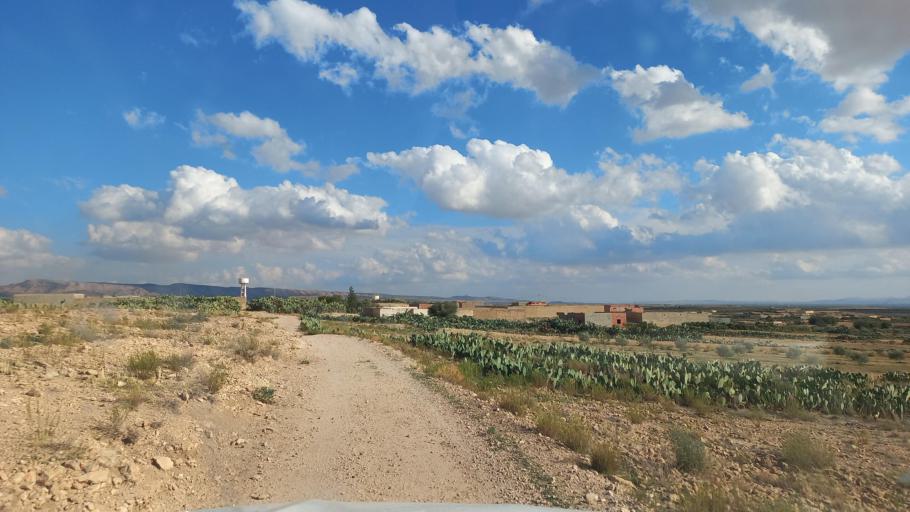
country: TN
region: Al Qasrayn
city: Sbiba
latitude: 35.3928
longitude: 9.0408
